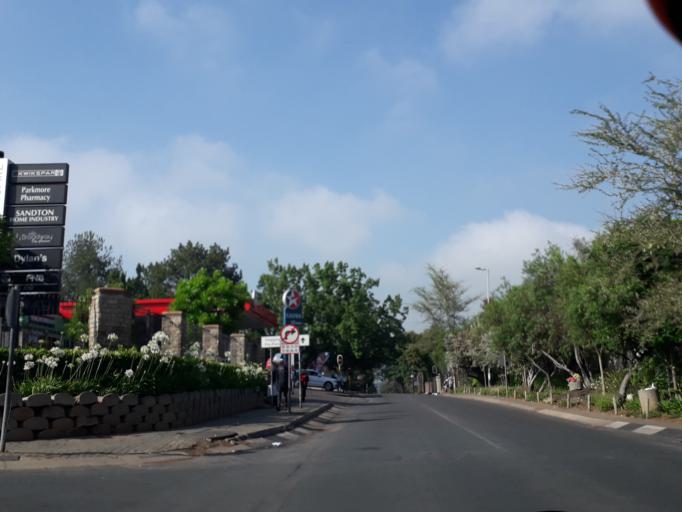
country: ZA
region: Gauteng
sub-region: City of Johannesburg Metropolitan Municipality
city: Johannesburg
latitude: -26.0924
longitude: 28.0362
